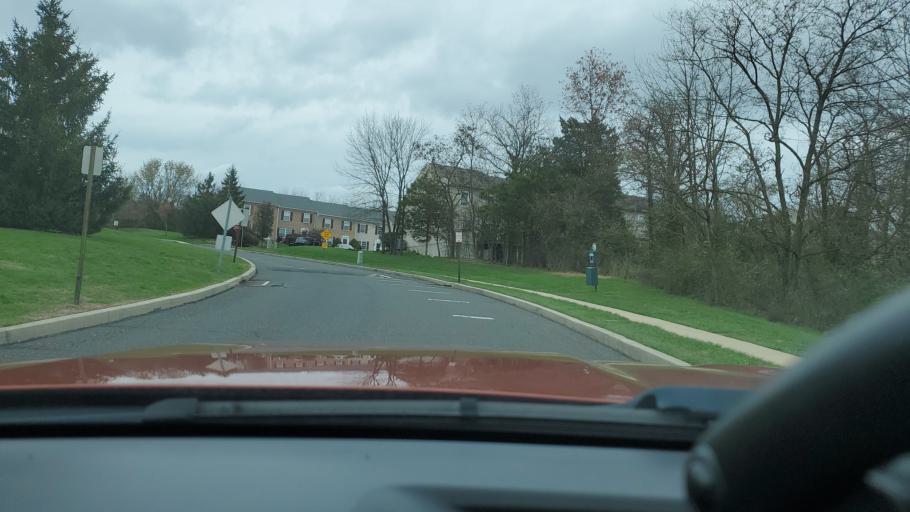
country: US
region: Pennsylvania
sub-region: Montgomery County
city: Woxall
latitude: 40.3033
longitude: -75.4929
